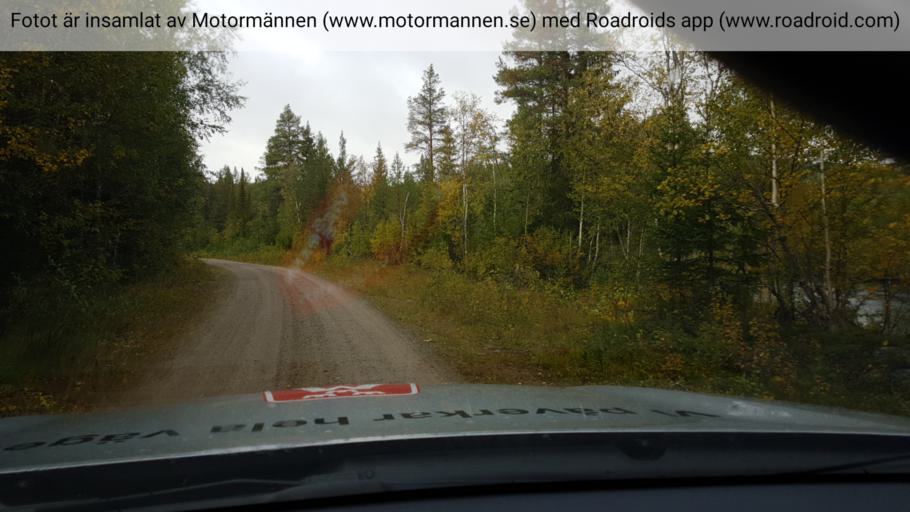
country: SE
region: Jaemtland
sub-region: Harjedalens Kommun
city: Sveg
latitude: 62.2491
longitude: 13.2887
